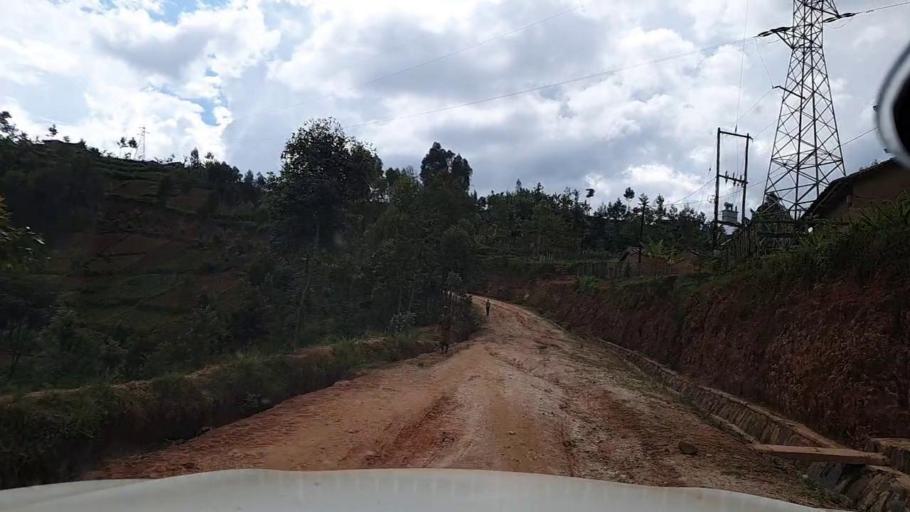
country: RW
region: Southern Province
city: Nzega
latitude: -2.7019
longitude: 29.4346
